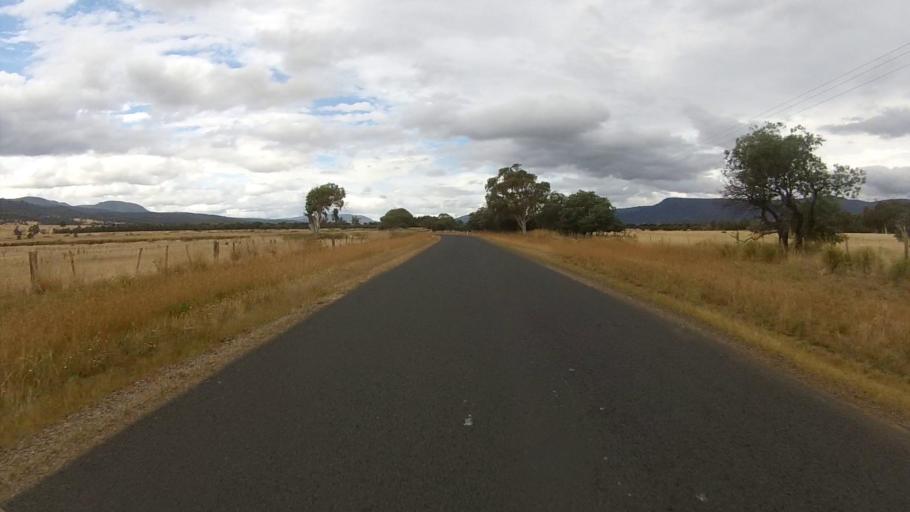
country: AU
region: Tasmania
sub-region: Northern Midlands
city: Evandale
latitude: -41.8238
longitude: 147.8223
